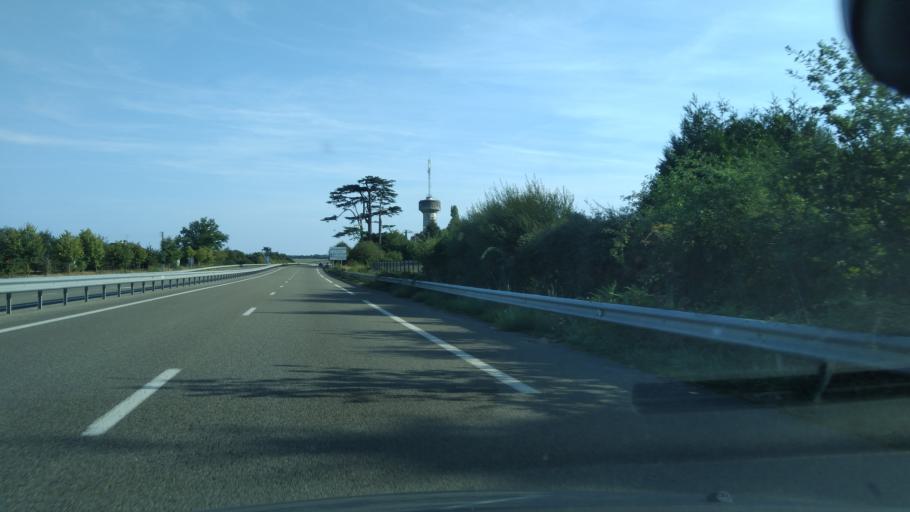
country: FR
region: Pays de la Loire
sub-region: Departement de la Mayenne
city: Entrammes
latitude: 48.0115
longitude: -0.7284
